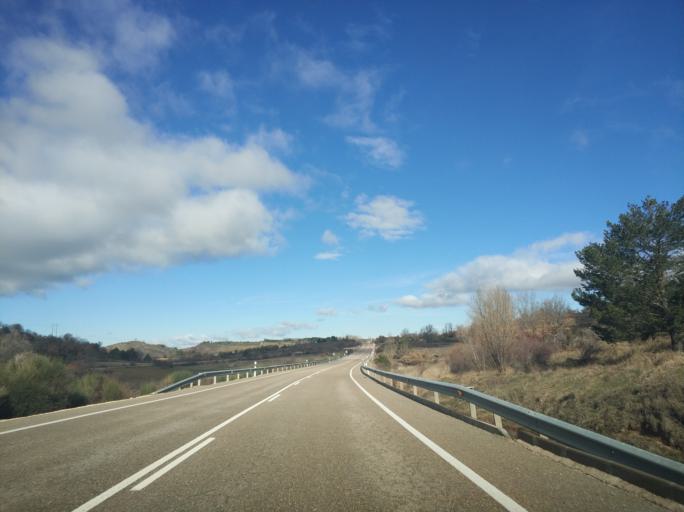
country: ES
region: Castille and Leon
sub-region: Provincia de Burgos
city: Cabezon de la Sierra
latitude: 41.8903
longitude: -3.2503
